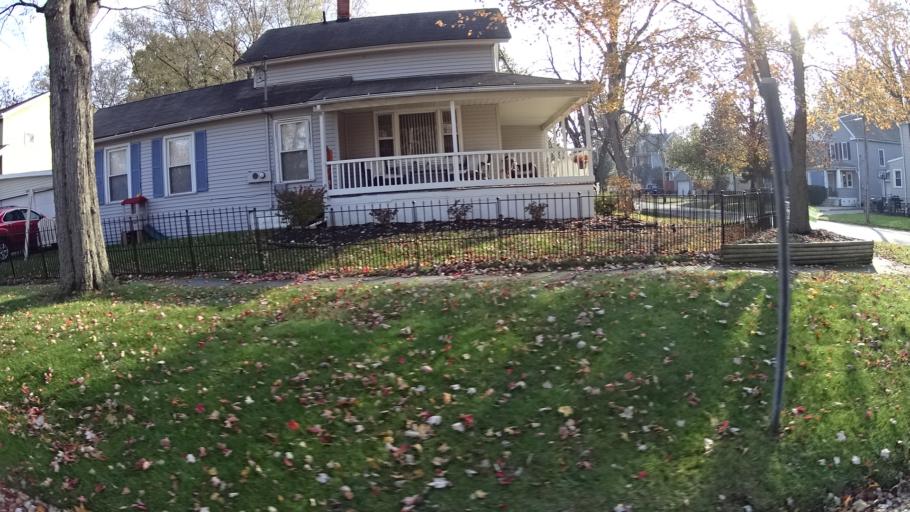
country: US
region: Ohio
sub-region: Lorain County
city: Elyria
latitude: 41.3741
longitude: -82.0998
